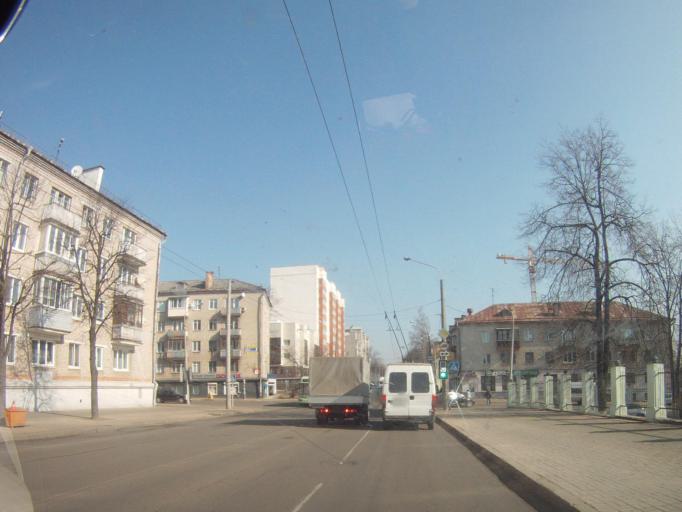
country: BY
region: Minsk
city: Minsk
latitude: 53.9272
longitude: 27.6053
